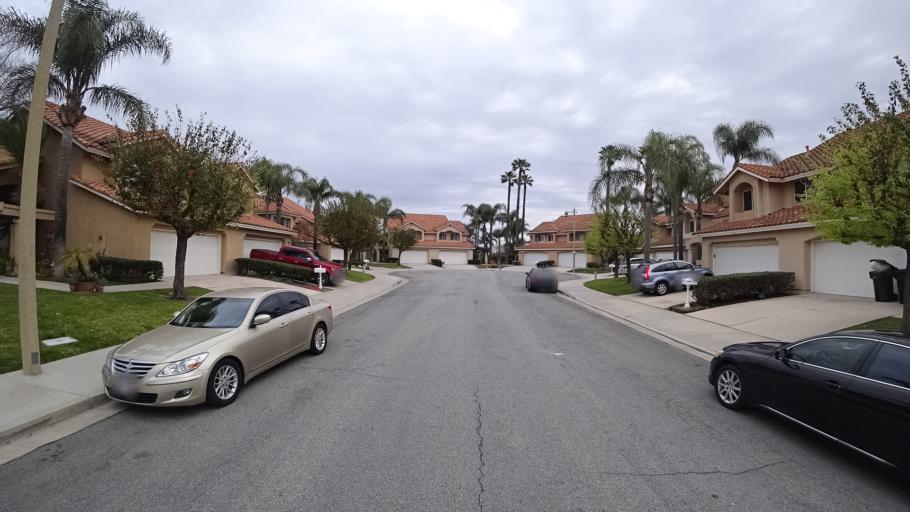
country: US
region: California
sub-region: Orange County
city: Villa Park
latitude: 33.8345
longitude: -117.7816
